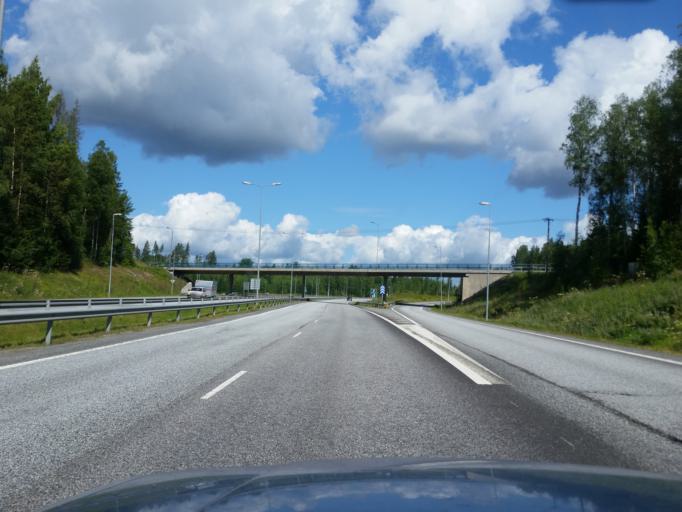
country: FI
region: Uusimaa
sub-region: Helsinki
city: Vihti
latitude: 60.3007
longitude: 24.3573
